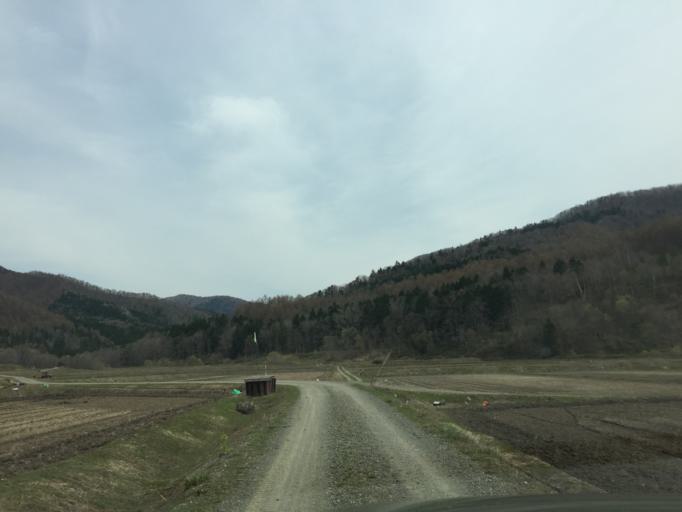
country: JP
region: Hokkaido
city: Ashibetsu
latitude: 43.6207
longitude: 142.2220
